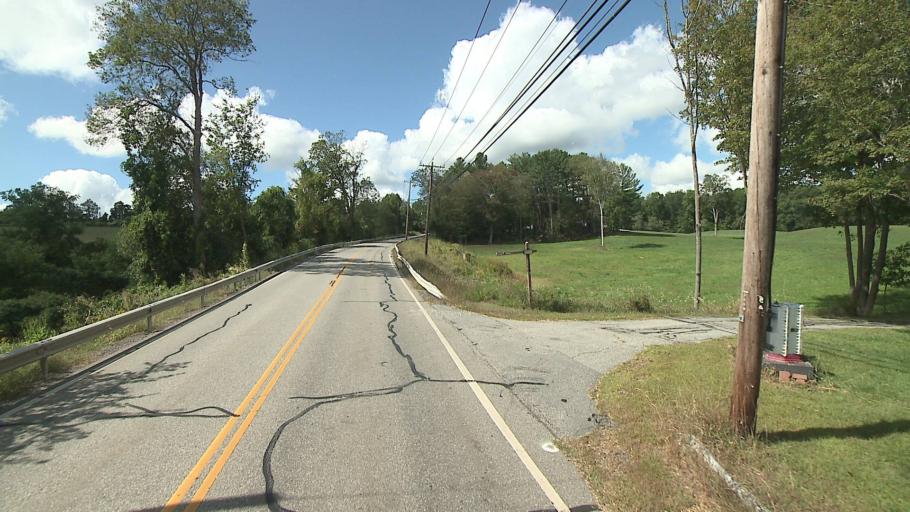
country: US
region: Connecticut
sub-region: Windham County
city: Putnam
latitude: 41.8967
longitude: -71.9445
